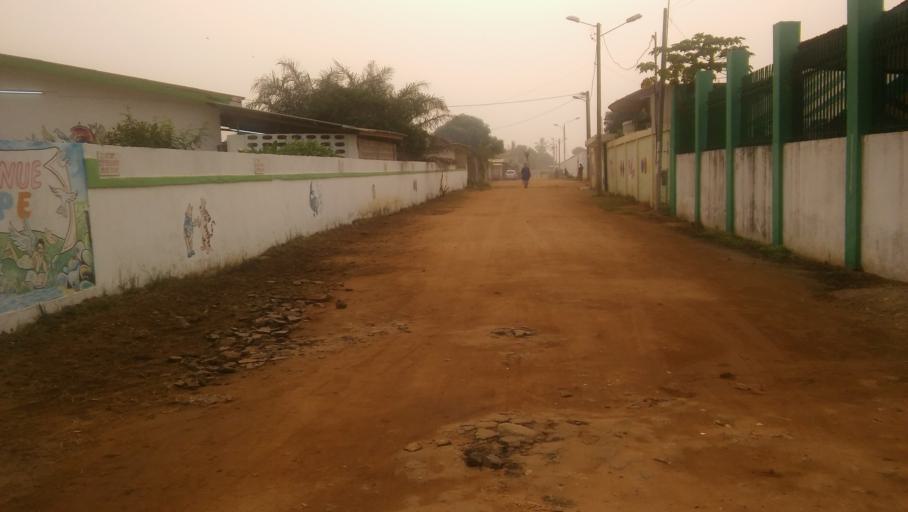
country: CI
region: Sud-Comoe
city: Grand-Bassam
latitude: 5.2032
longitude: -3.7359
